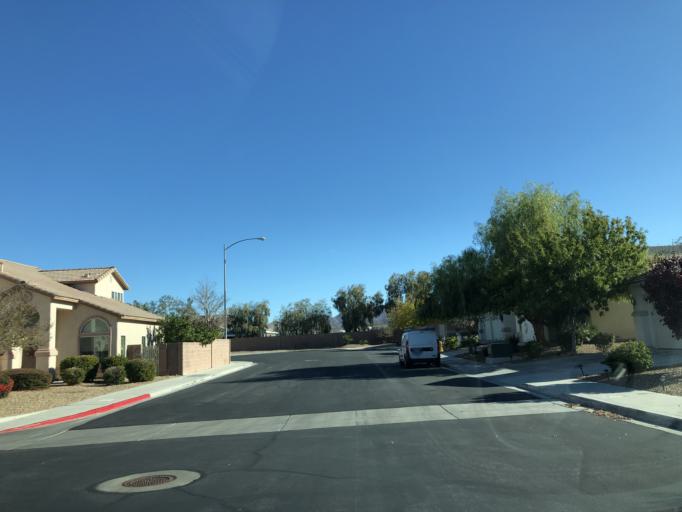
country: US
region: Nevada
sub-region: Clark County
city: Whitney
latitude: 36.0009
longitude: -115.0886
